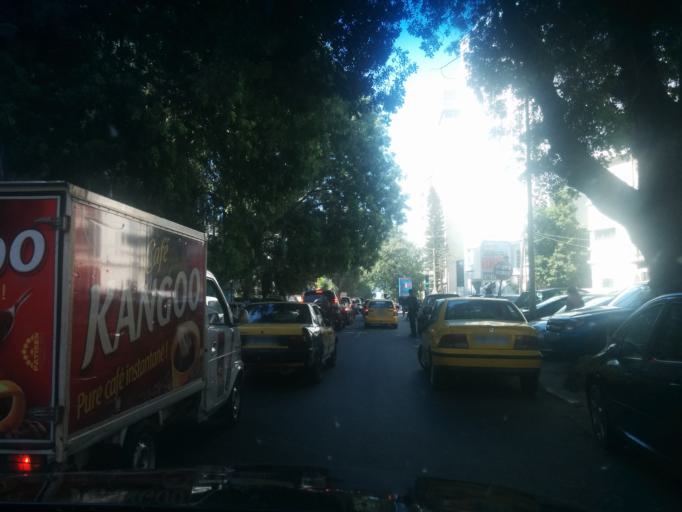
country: SN
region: Dakar
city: Dakar
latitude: 14.6665
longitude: -17.4397
